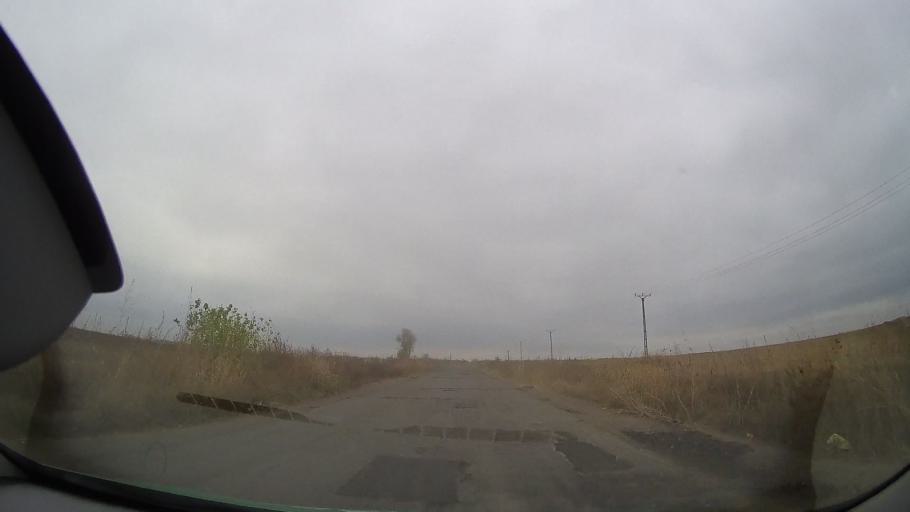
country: RO
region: Braila
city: Dudesti
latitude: 44.9317
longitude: 27.4271
